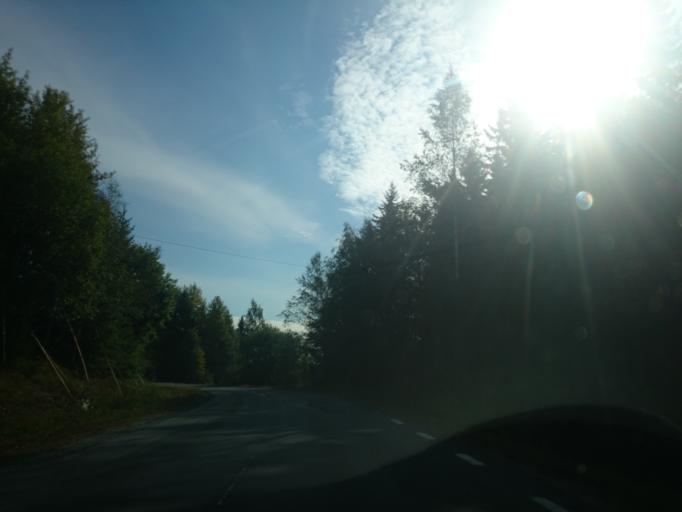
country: SE
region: Vaesternorrland
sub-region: Kramfors Kommun
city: Nordingra
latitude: 62.9346
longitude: 18.2306
